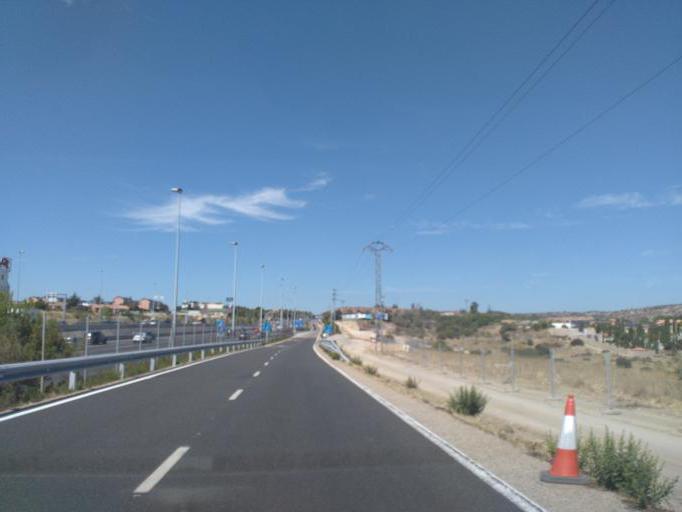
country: ES
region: Madrid
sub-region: Provincia de Madrid
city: Torrelodones
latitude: 40.5686
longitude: -3.9164
